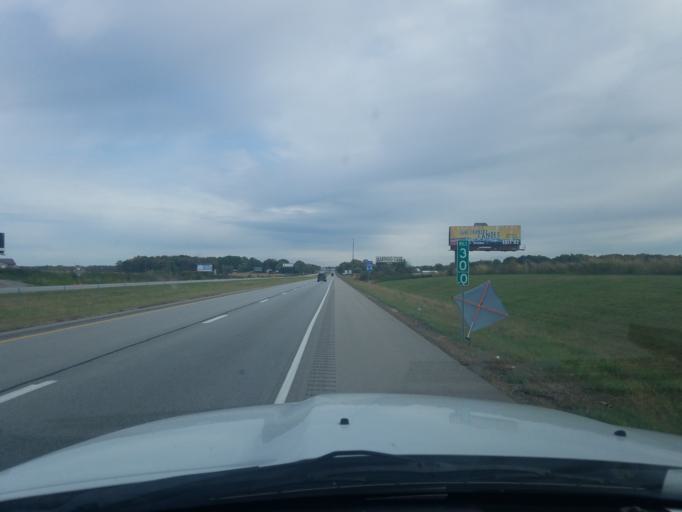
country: US
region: Indiana
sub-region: Gibson County
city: Haubstadt
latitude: 38.1696
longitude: -87.4599
